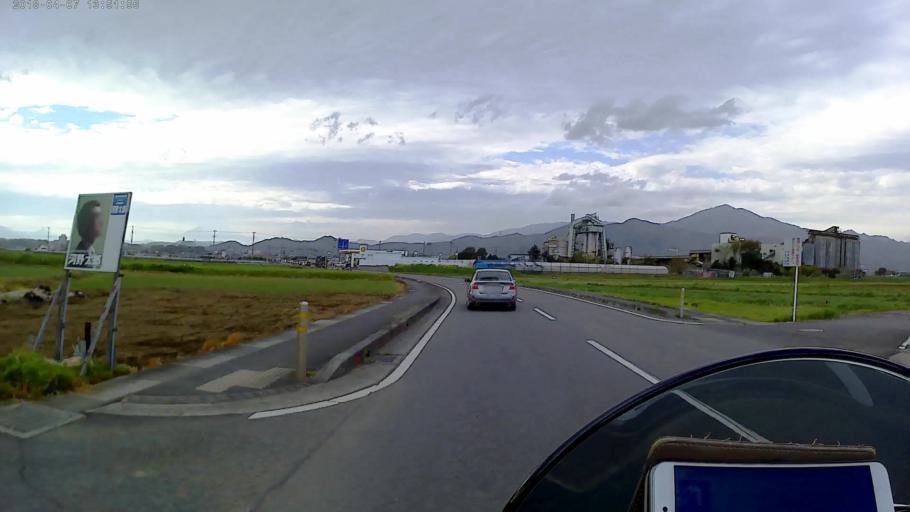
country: JP
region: Kanagawa
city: Isehara
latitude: 35.3669
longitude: 139.3009
